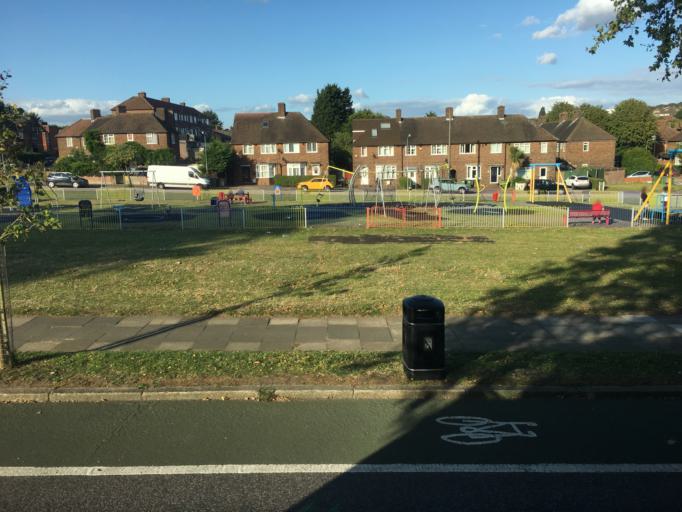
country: GB
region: England
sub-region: Greater London
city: Blackheath
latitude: 51.4627
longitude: 0.0379
